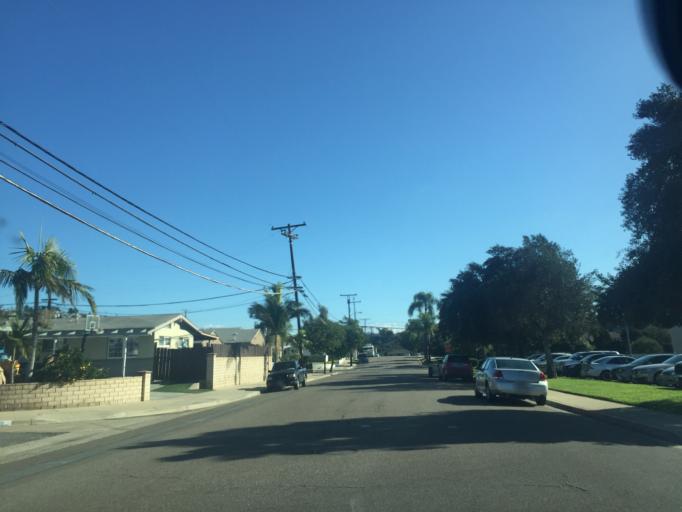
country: US
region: California
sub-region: San Diego County
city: La Mesa
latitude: 32.7923
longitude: -117.0801
